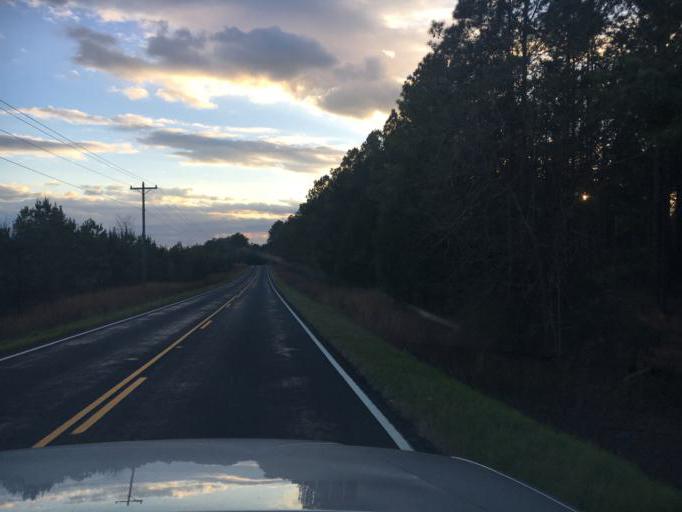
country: US
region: South Carolina
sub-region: Greenwood County
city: Greenwood
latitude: 34.0809
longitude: -82.2133
